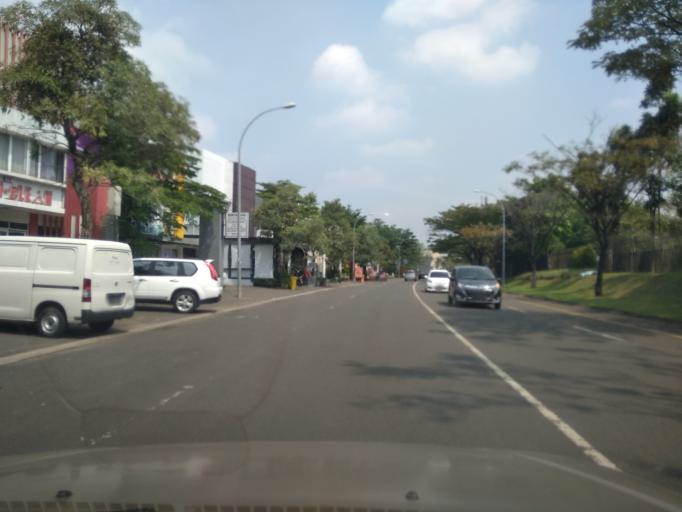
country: ID
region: West Java
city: Serpong
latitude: -6.3133
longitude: 106.6513
